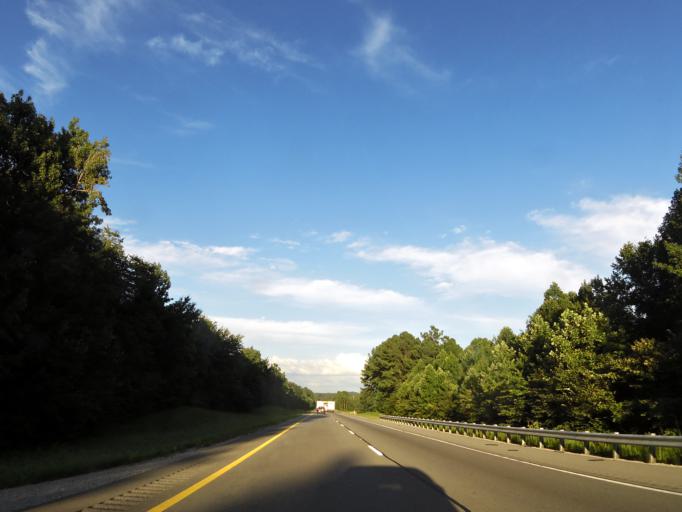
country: US
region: Tennessee
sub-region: Putnam County
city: Baxter
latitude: 36.1399
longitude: -85.5894
